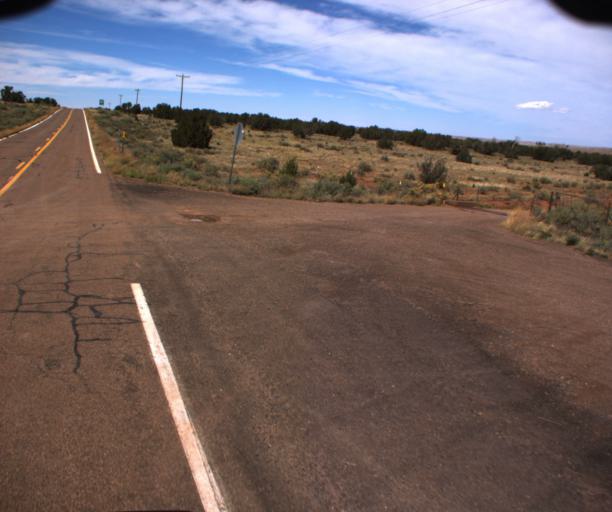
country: US
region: Arizona
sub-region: Apache County
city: Saint Johns
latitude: 34.6116
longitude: -109.6585
